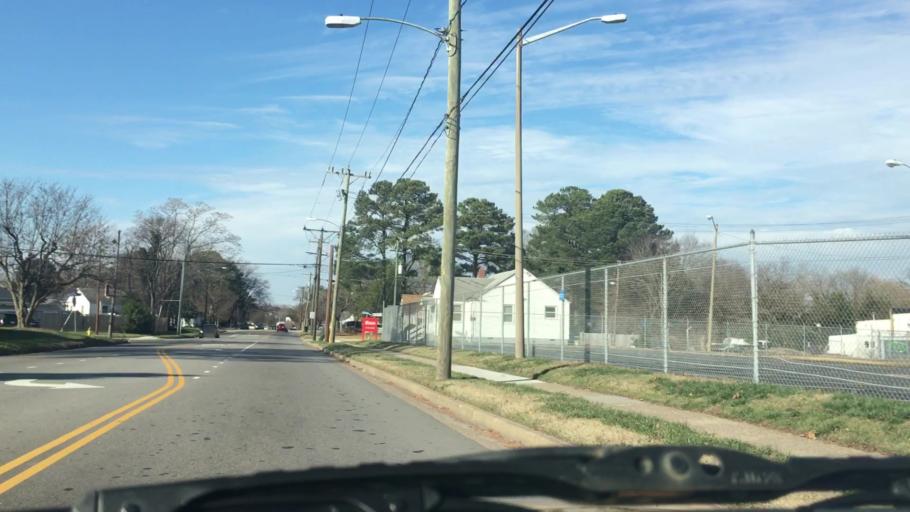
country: US
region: Virginia
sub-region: City of Norfolk
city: Norfolk
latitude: 36.8808
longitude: -76.2550
